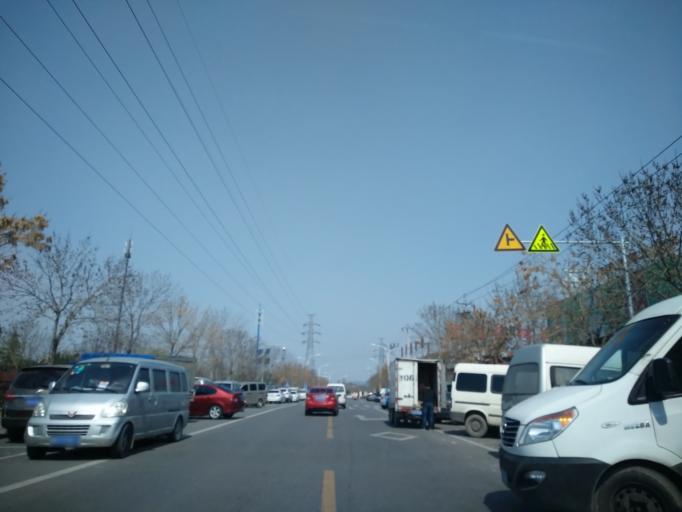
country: CN
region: Beijing
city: Qingyundian
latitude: 39.7568
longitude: 116.5345
